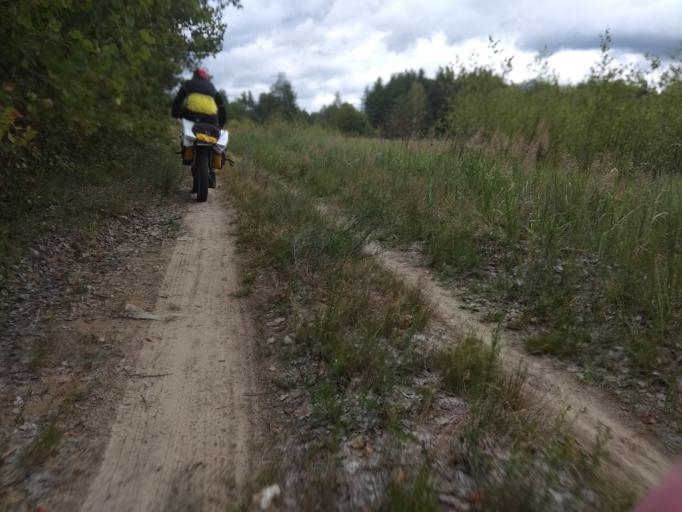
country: RU
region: Moskovskaya
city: Kerva
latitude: 55.5773
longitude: 39.6869
